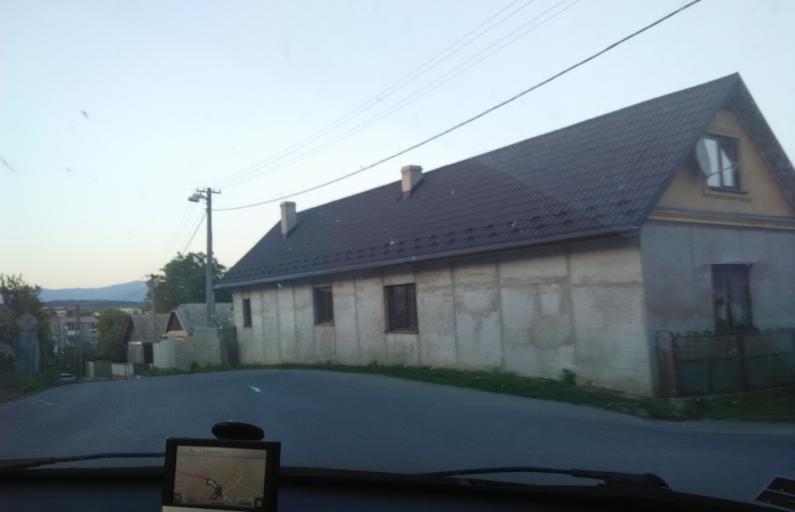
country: SK
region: Presovsky
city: Sabinov
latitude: 49.0565
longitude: 21.0614
